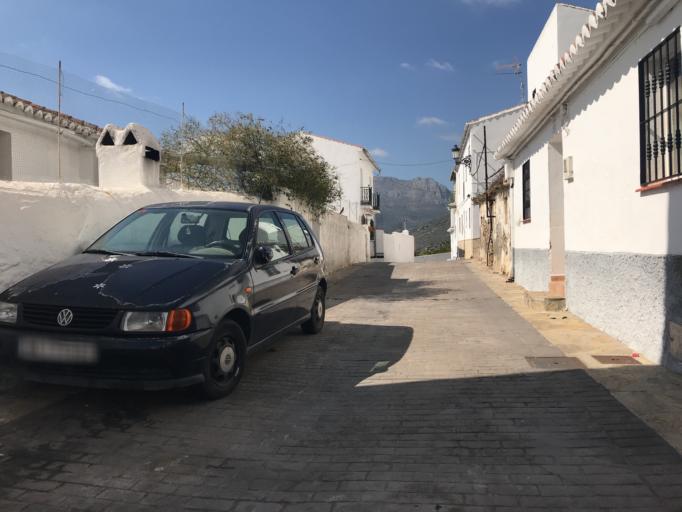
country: ES
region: Andalusia
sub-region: Provincia de Malaga
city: Alcaucin
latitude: 36.9032
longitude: -4.1131
